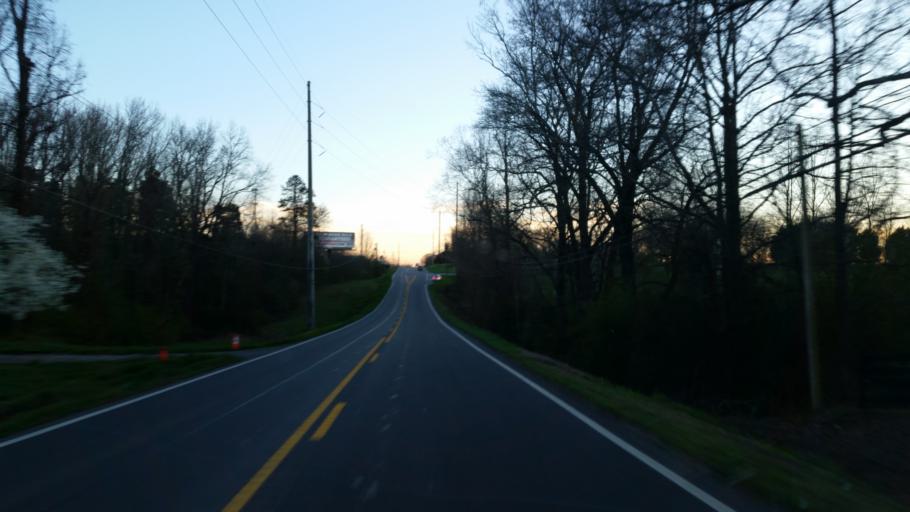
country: US
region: Georgia
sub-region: Forsyth County
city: Cumming
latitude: 34.2788
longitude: -84.0469
